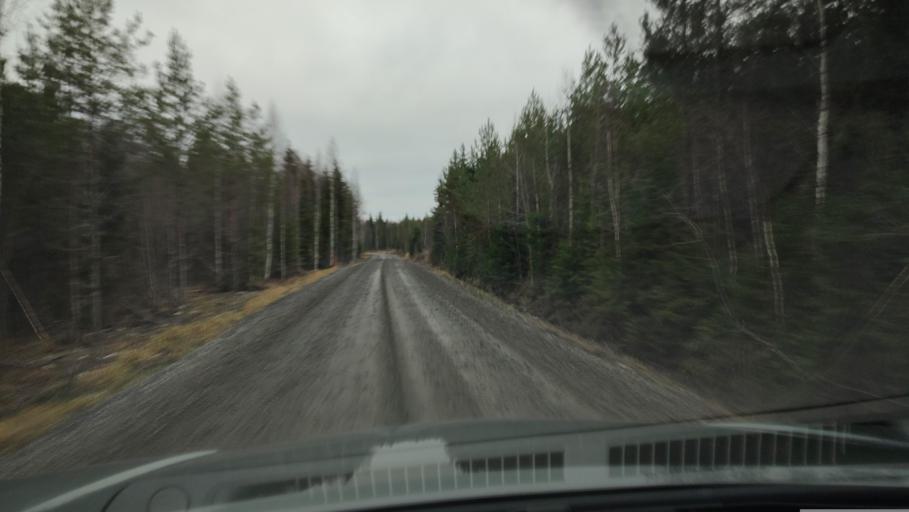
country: FI
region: Southern Ostrobothnia
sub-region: Suupohja
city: Karijoki
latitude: 62.1967
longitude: 21.5750
